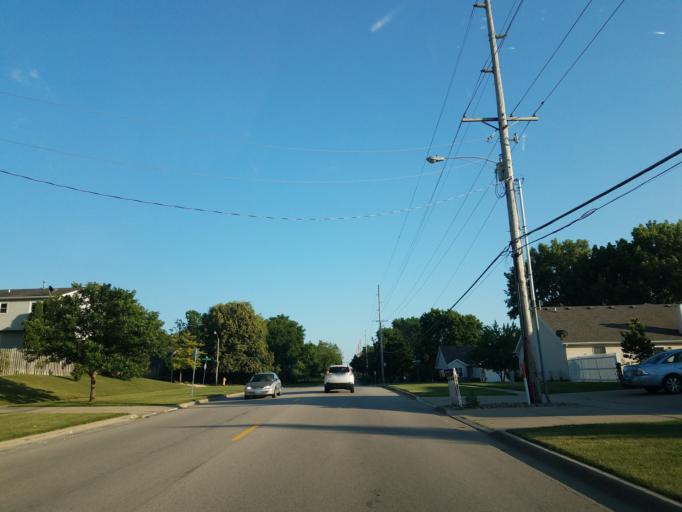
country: US
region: Illinois
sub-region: McLean County
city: Bloomington
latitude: 40.4550
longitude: -89.0059
